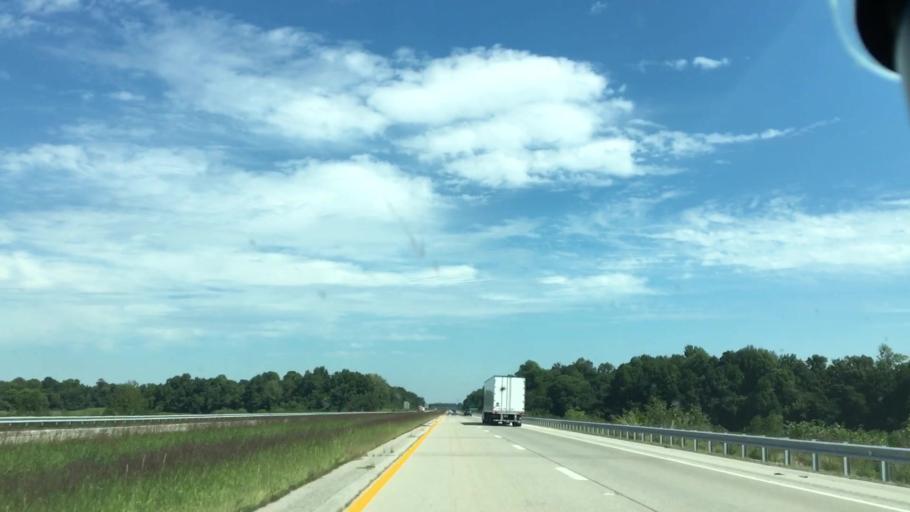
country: US
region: Kentucky
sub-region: Daviess County
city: Owensboro
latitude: 37.7595
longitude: -87.2460
